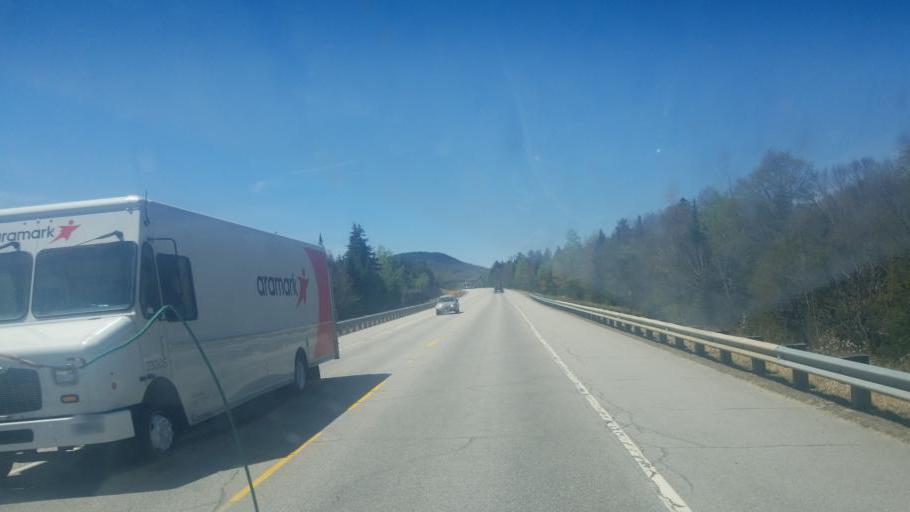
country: US
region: New Hampshire
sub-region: Grafton County
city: Deerfield
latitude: 44.2691
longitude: -71.4768
